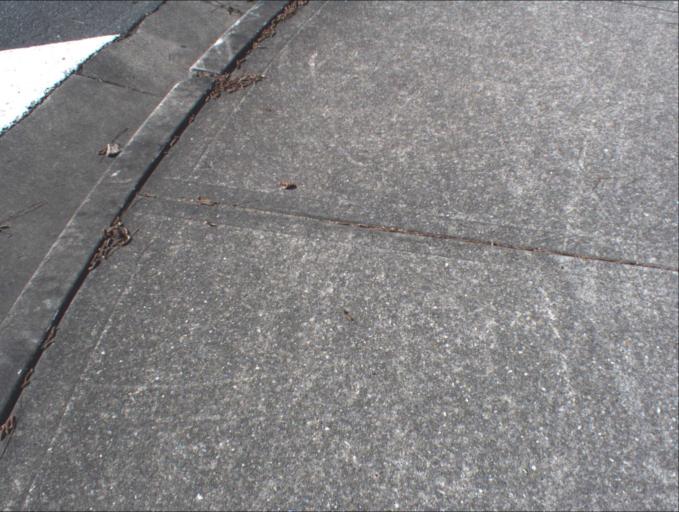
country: AU
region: Queensland
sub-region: Logan
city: Waterford West
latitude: -27.6953
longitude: 153.1462
